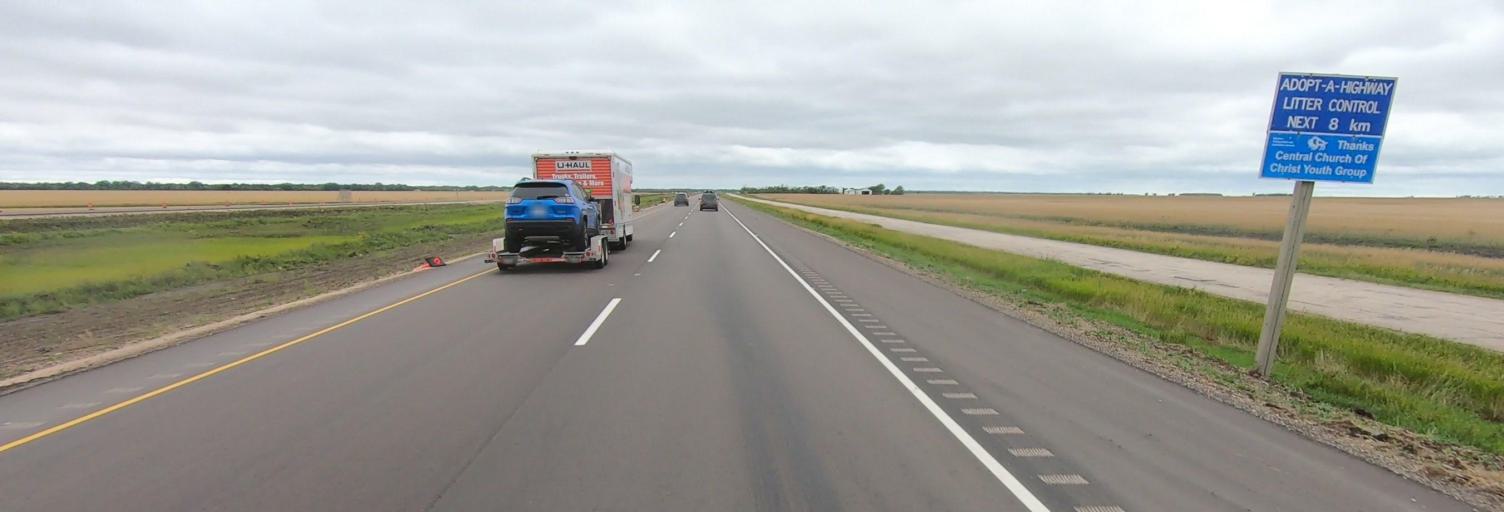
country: CA
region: Manitoba
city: Headingley
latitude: 49.8797
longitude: -97.4395
